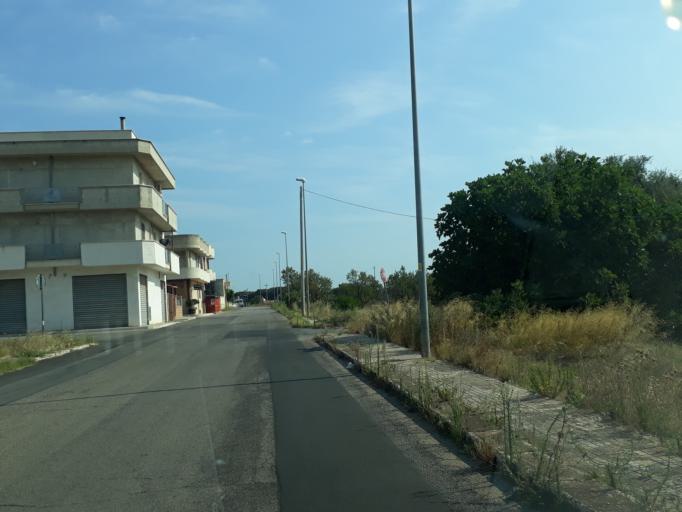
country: IT
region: Apulia
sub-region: Provincia di Brindisi
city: Carovigno
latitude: 40.6992
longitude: 17.6674
